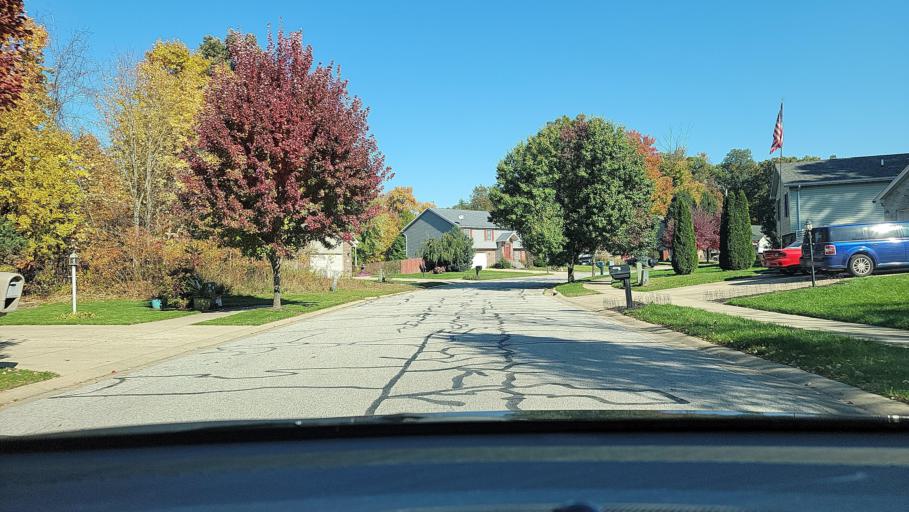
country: US
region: Indiana
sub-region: Porter County
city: Portage
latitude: 41.5783
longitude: -87.1574
